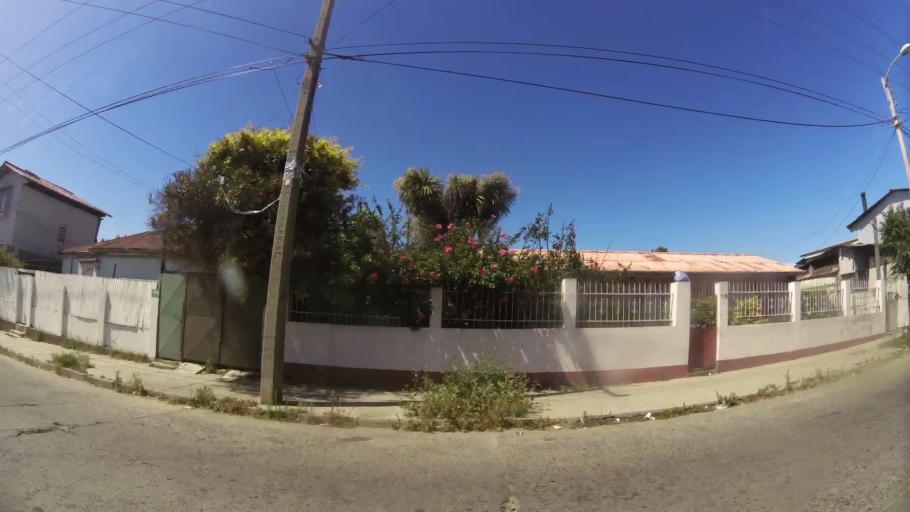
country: CL
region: Valparaiso
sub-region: Provincia de Valparaiso
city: Valparaiso
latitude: -33.0490
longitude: -71.5927
